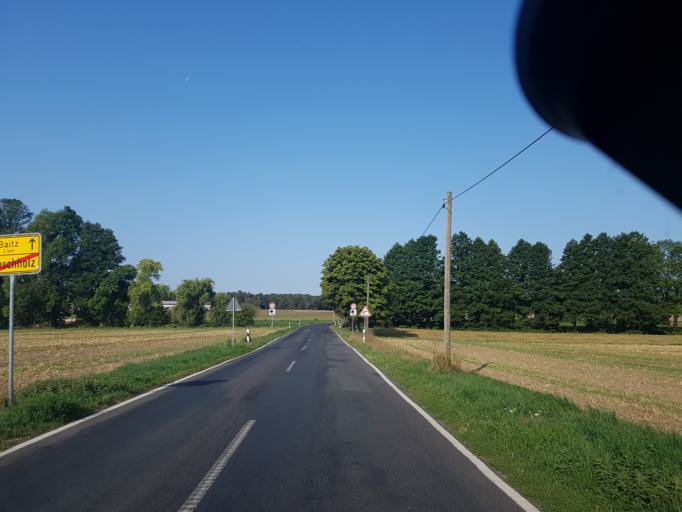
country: DE
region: Brandenburg
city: Niemegk
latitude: 52.1552
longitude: 12.6936
